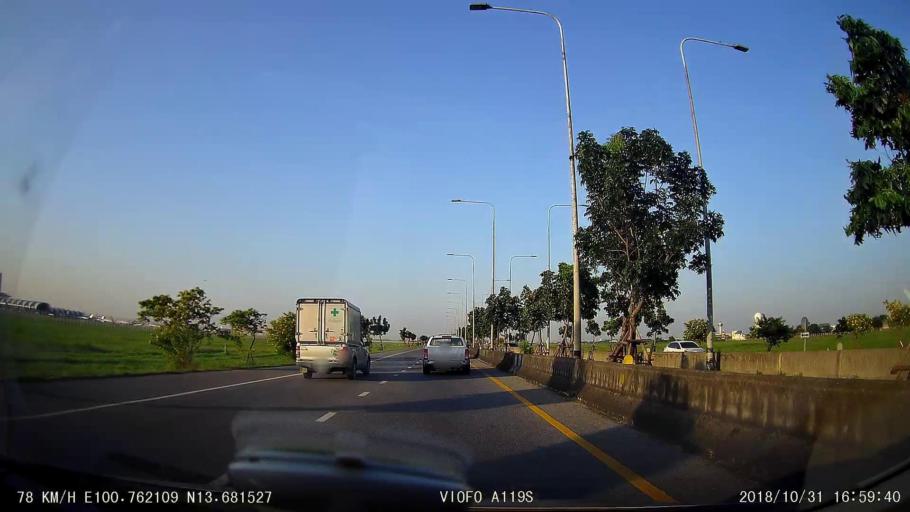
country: TH
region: Bangkok
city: Lat Krabang
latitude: 13.6818
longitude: 100.7622
